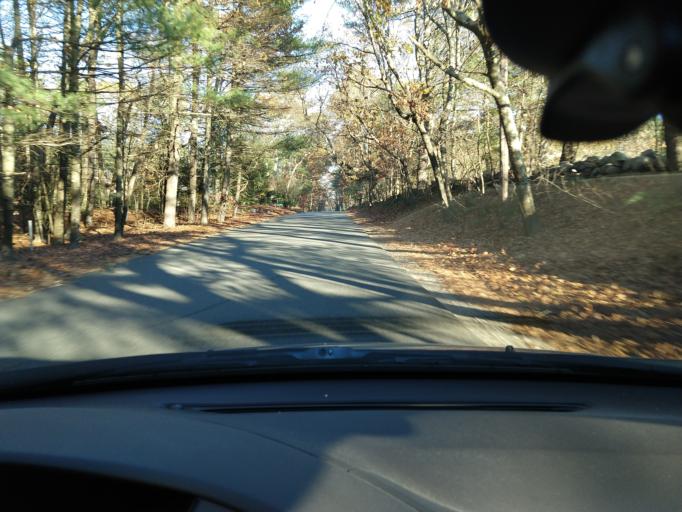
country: US
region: Massachusetts
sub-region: Middlesex County
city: Carlisle
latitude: 42.5098
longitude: -71.3192
